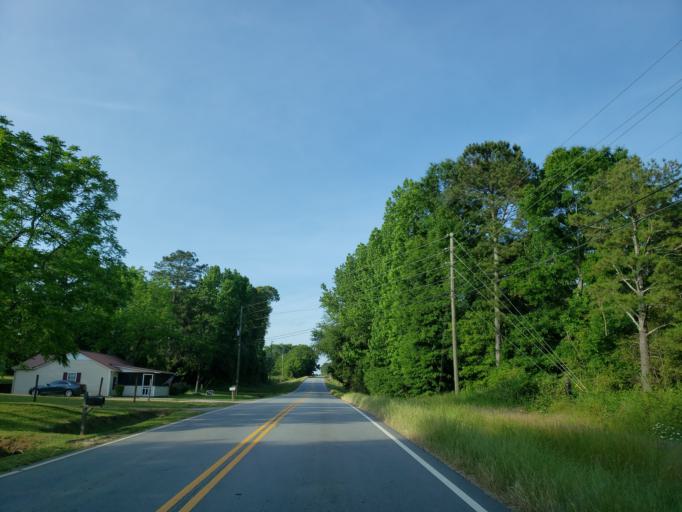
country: US
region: Georgia
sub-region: Carroll County
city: Bowdon
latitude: 33.5136
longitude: -85.2635
